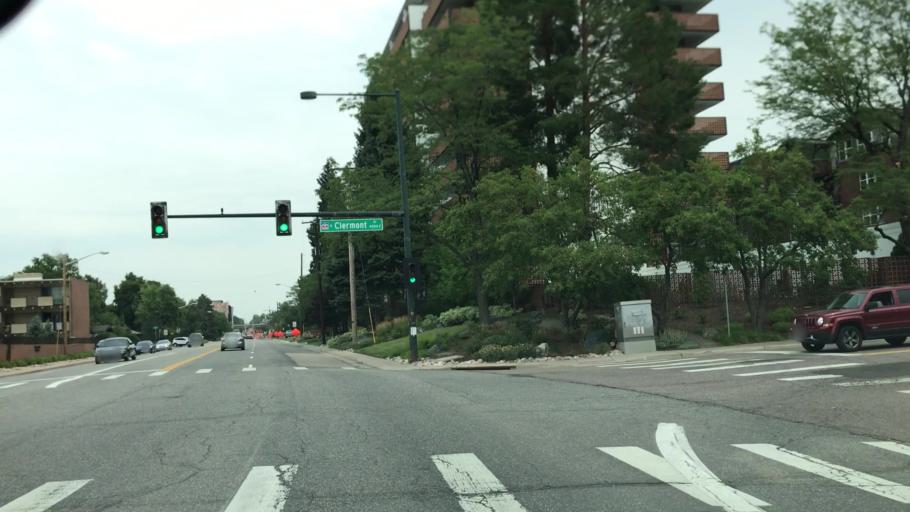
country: US
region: Colorado
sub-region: Arapahoe County
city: Cherry Hills Village
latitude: 39.6675
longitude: -104.9364
